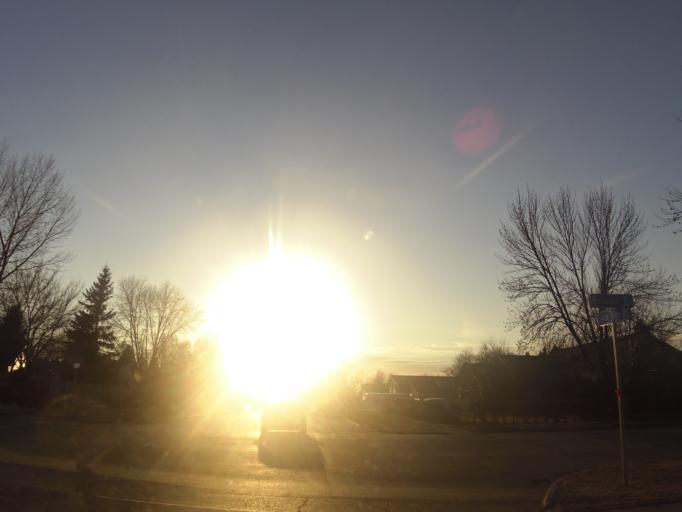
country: US
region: North Dakota
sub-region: Grand Forks County
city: Grand Forks
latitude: 47.8809
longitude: -97.0289
